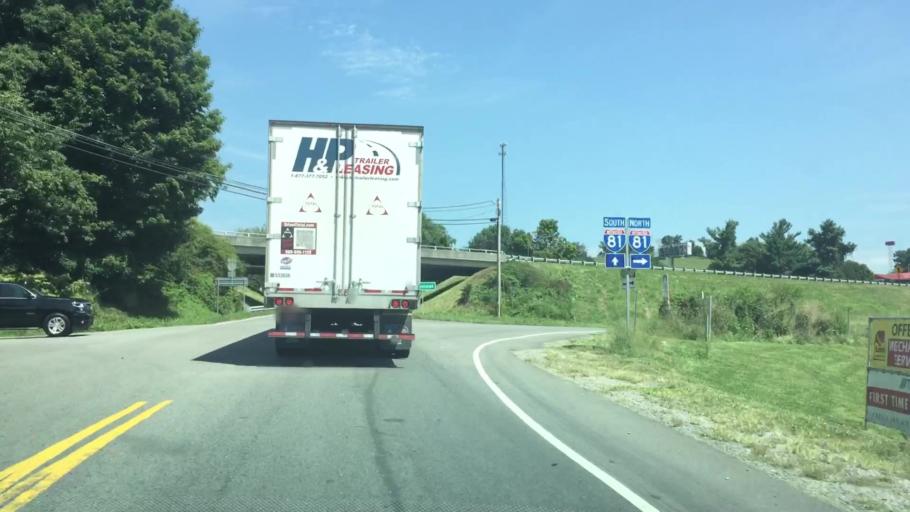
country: US
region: Virginia
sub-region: Washington County
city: Emory
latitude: 36.7566
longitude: -81.8571
